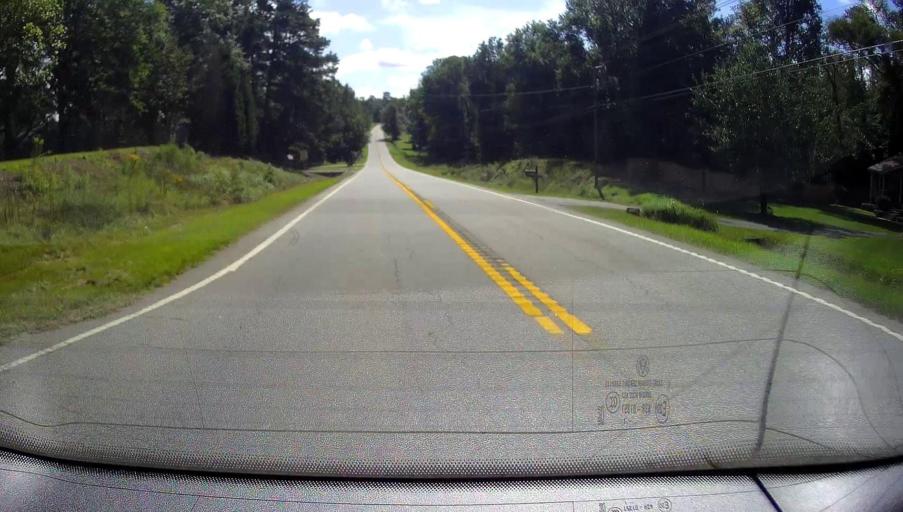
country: US
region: Georgia
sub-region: Bibb County
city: Macon
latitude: 32.8202
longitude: -83.5703
